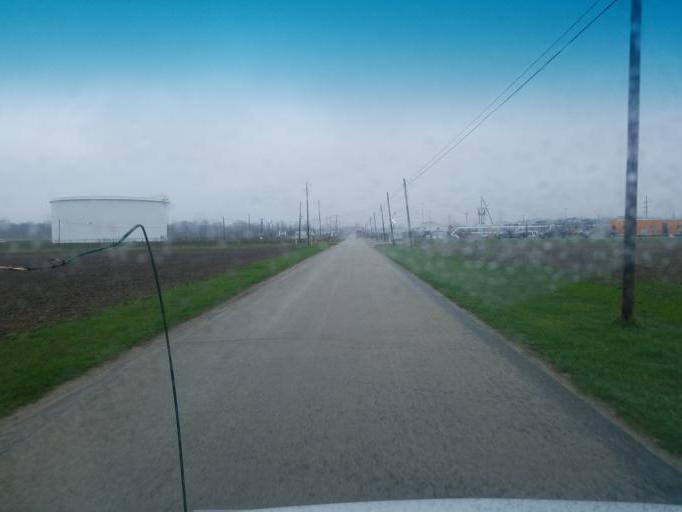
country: US
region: Ohio
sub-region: Wood County
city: North Baltimore
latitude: 41.2302
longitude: -83.6403
